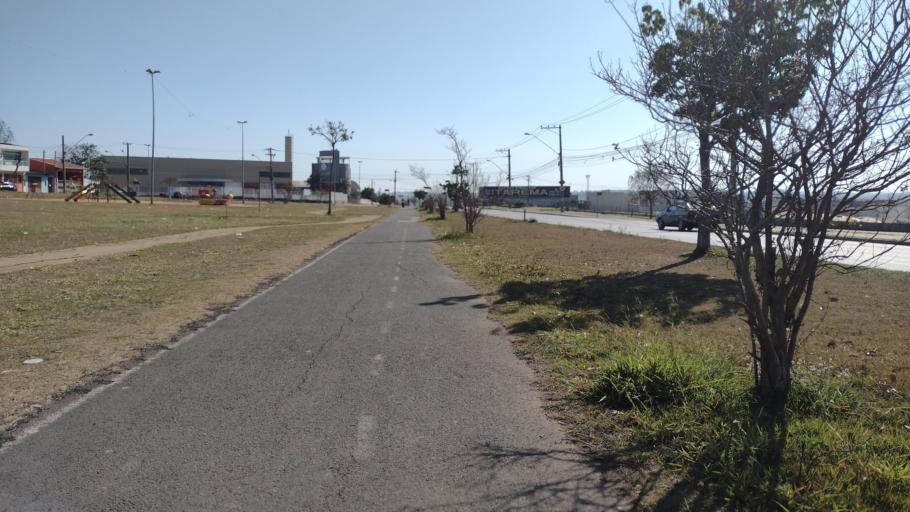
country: BR
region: Sao Paulo
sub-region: Sorocaba
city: Sorocaba
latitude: -23.4251
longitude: -47.4828
